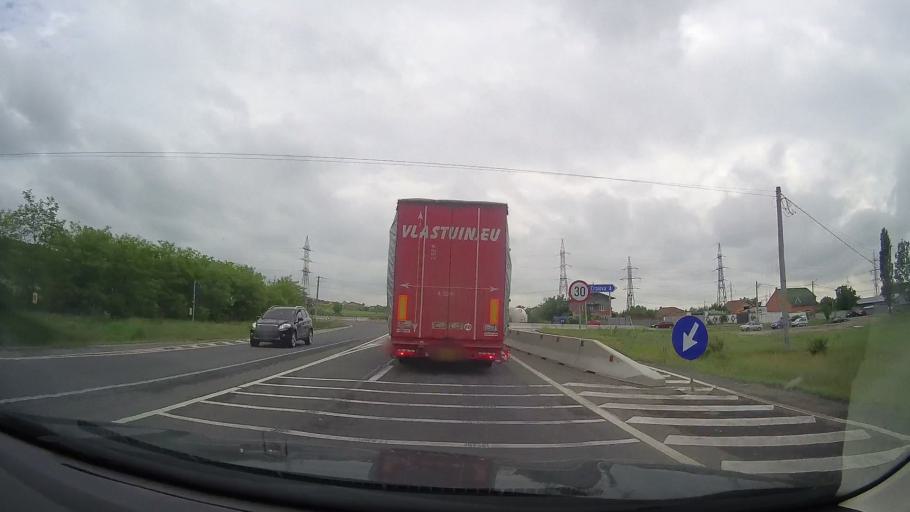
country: RO
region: Dolj
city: Craiova
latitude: 44.3367
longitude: 23.8398
